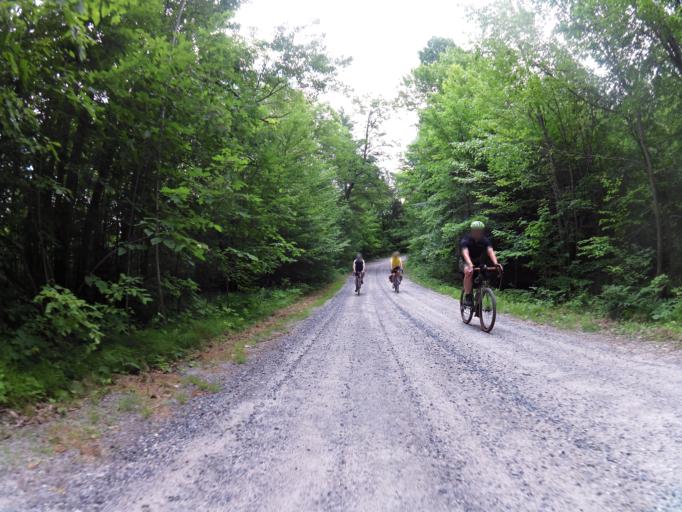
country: CA
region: Ontario
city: Perth
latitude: 45.0265
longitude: -76.5375
